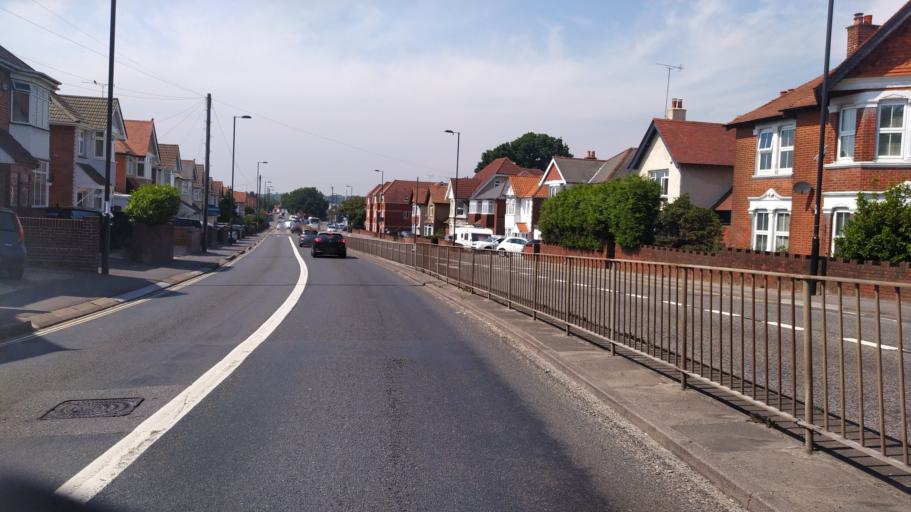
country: GB
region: England
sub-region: Southampton
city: Southampton
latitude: 50.9172
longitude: -1.3714
